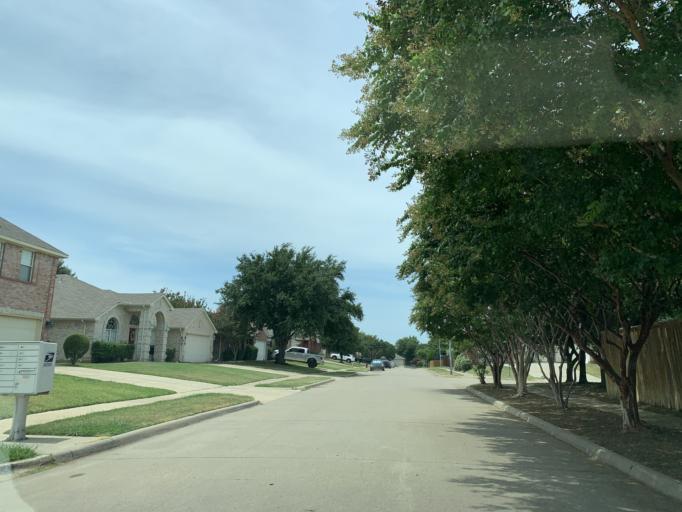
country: US
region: Texas
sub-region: Dallas County
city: Grand Prairie
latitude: 32.6619
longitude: -97.0213
